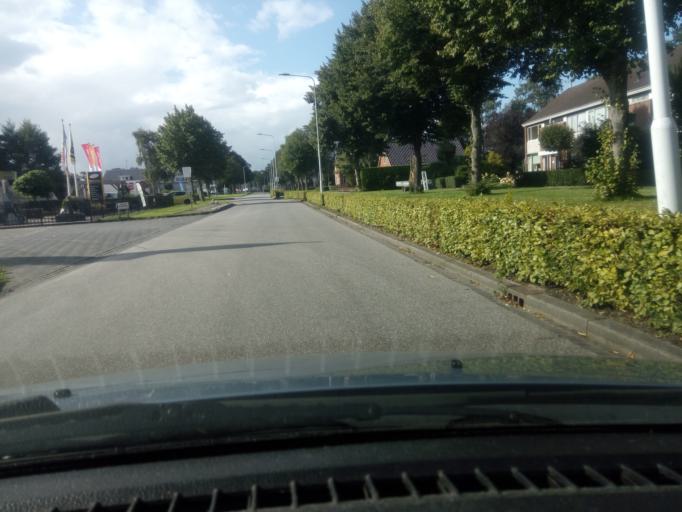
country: NL
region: Friesland
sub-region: Gemeente Achtkarspelen
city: Surhuisterveen
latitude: 53.1824
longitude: 6.1796
